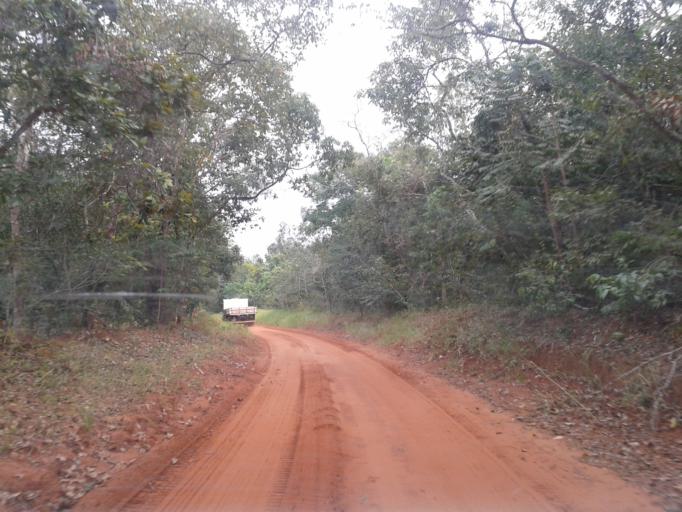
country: BR
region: Minas Gerais
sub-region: Campina Verde
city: Campina Verde
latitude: -19.4034
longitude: -49.6362
